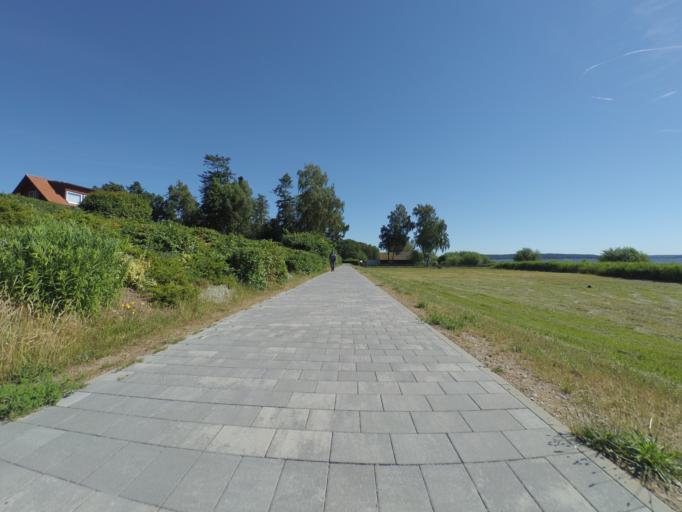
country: DE
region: Mecklenburg-Vorpommern
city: Plau am See
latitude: 53.4706
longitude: 12.2860
